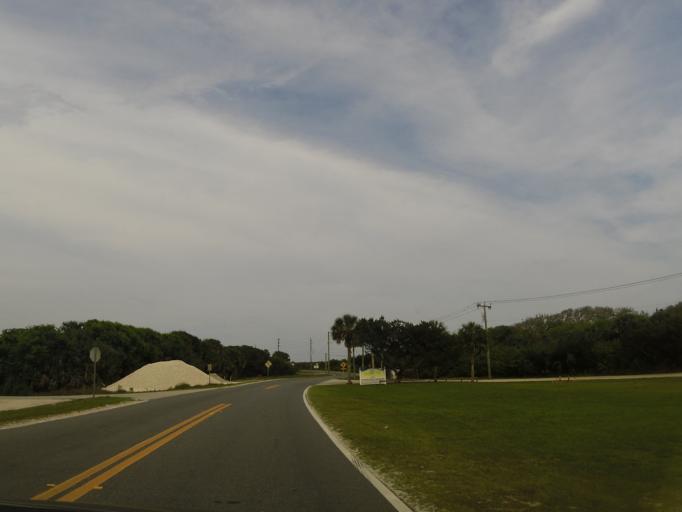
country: US
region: Florida
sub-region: Volusia County
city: Ormond-by-the-Sea
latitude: 29.4091
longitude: -81.0996
